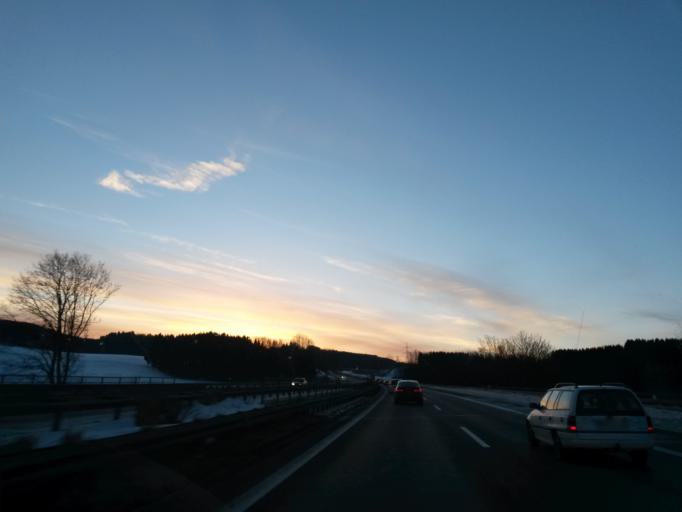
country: DE
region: Bavaria
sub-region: Swabia
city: Wolfertschwenden
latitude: 47.8708
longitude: 10.2552
